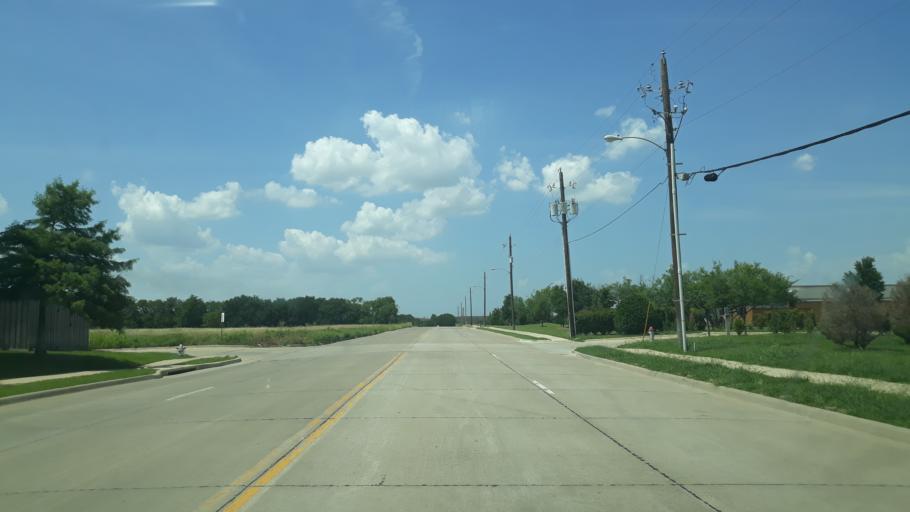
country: US
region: Texas
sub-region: Dallas County
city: Coppell
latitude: 32.9567
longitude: -97.0365
